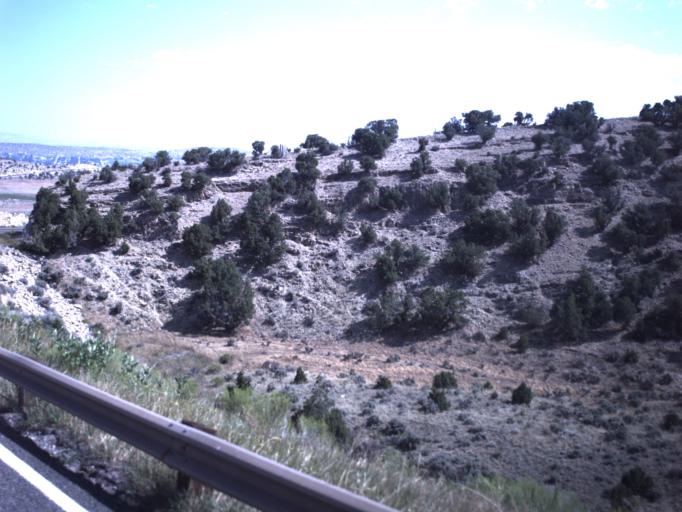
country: US
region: Utah
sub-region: Daggett County
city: Manila
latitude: 40.9399
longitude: -109.7133
